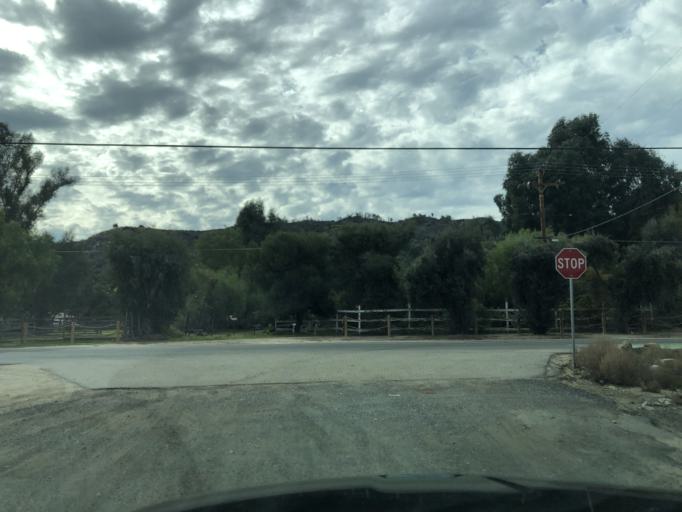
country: US
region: California
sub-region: Riverside County
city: Wildomar
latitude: 33.6065
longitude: -117.2917
